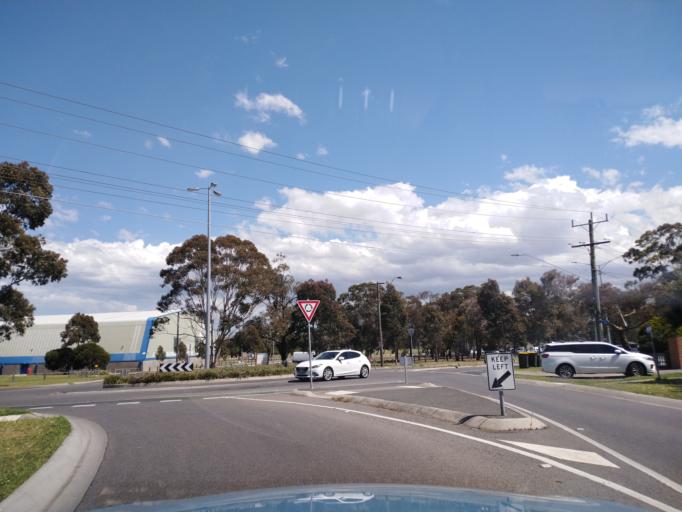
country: AU
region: Victoria
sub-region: Hobsons Bay
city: Altona North
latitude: -37.8395
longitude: 144.8589
